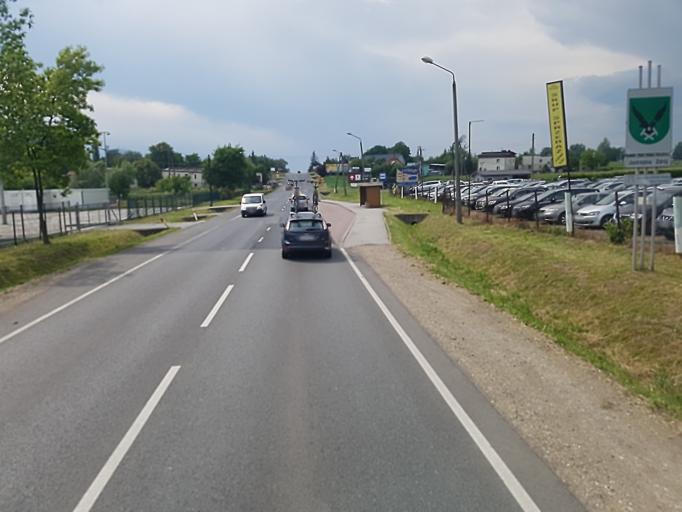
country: PL
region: Silesian Voivodeship
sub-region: Powiat pszczynski
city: Krzyzowice
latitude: 49.9583
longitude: 18.6784
